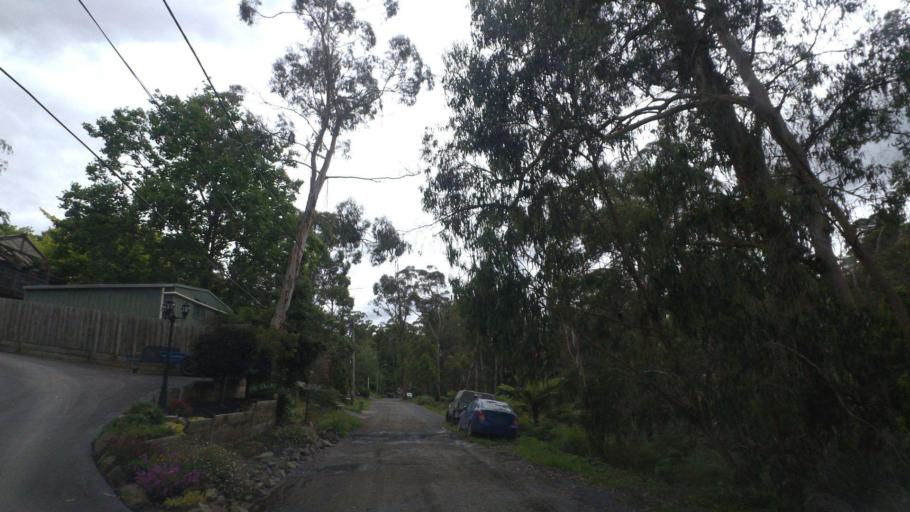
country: AU
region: Victoria
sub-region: Yarra Ranges
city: Mount Evelyn
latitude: -37.7879
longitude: 145.3671
